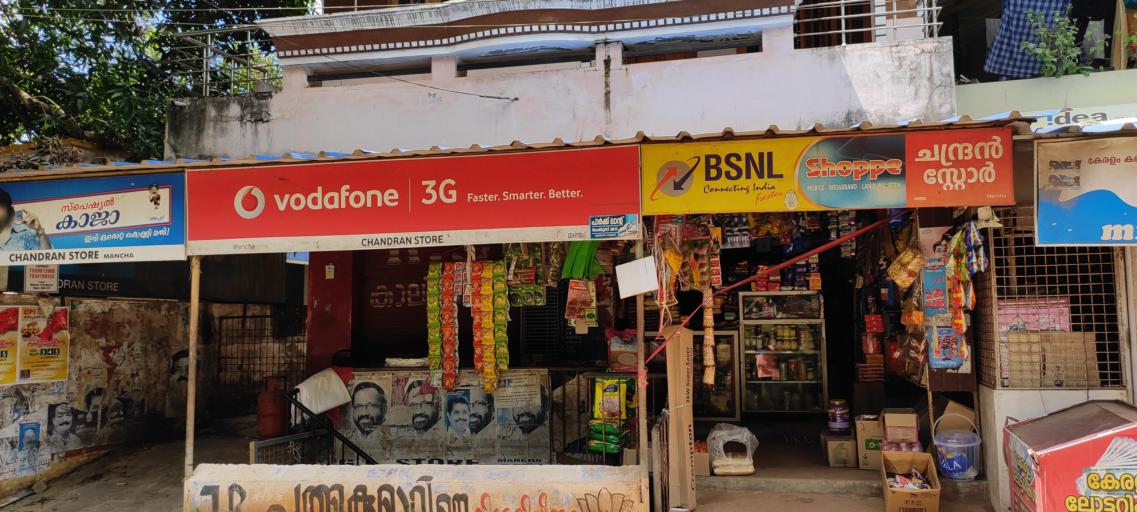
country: IN
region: Kerala
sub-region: Thiruvananthapuram
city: Nedumangad
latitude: 8.5962
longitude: 77.0093
